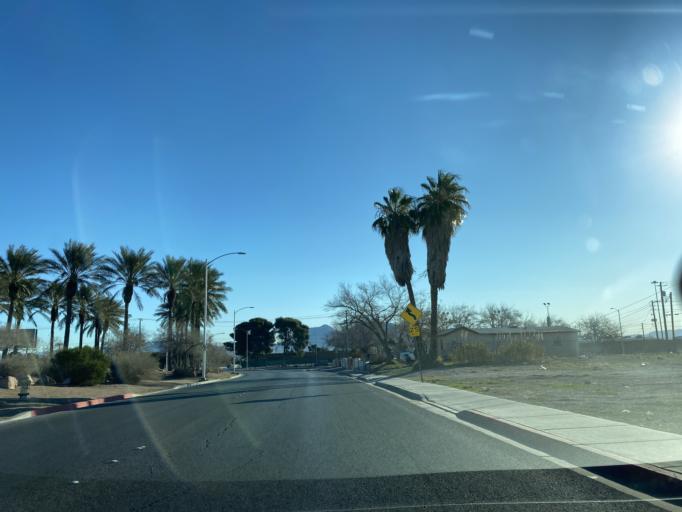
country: US
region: Nevada
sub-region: Clark County
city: Las Vegas
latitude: 36.1880
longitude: -115.1459
